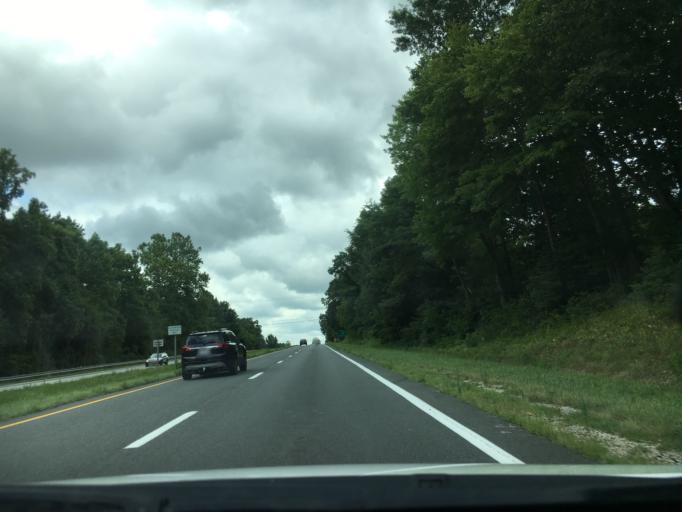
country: US
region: Virginia
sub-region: Amherst County
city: Amherst
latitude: 37.5914
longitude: -79.0350
